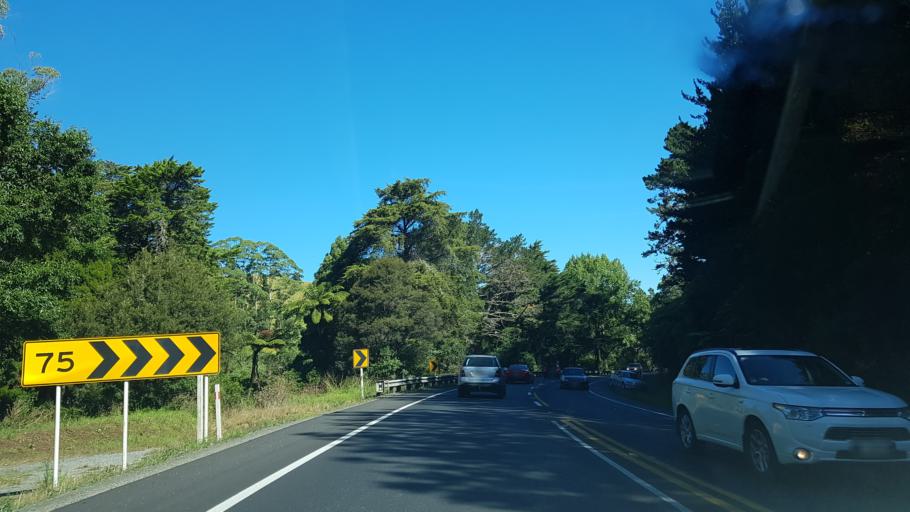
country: NZ
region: Auckland
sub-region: Auckland
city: Warkworth
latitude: -36.4423
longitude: 174.6503
